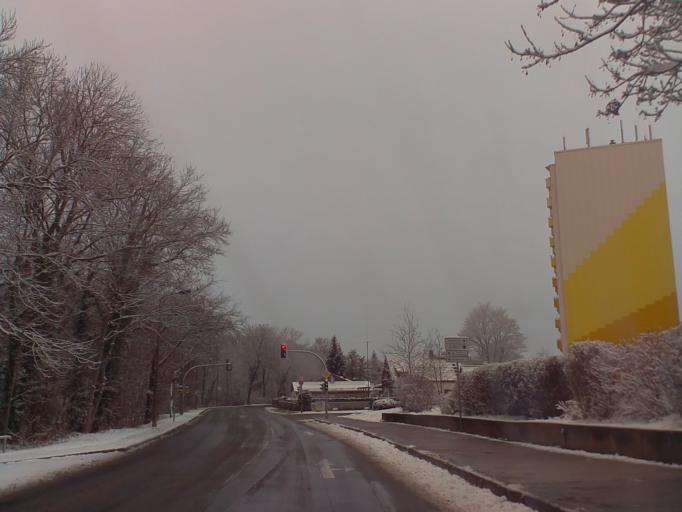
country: DE
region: Thuringia
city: Arnstadt
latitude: 50.8340
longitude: 10.9564
